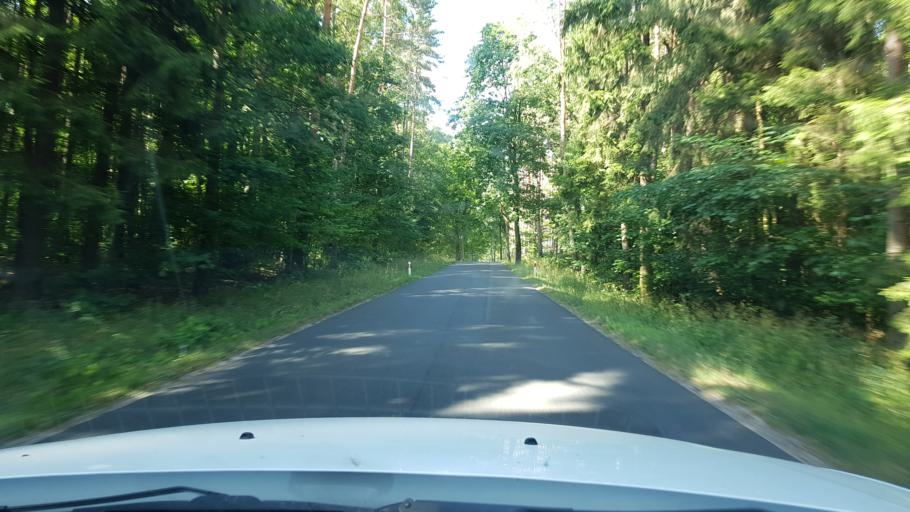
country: PL
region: West Pomeranian Voivodeship
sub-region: Powiat drawski
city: Zlocieniec
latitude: 53.5716
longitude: 16.0096
